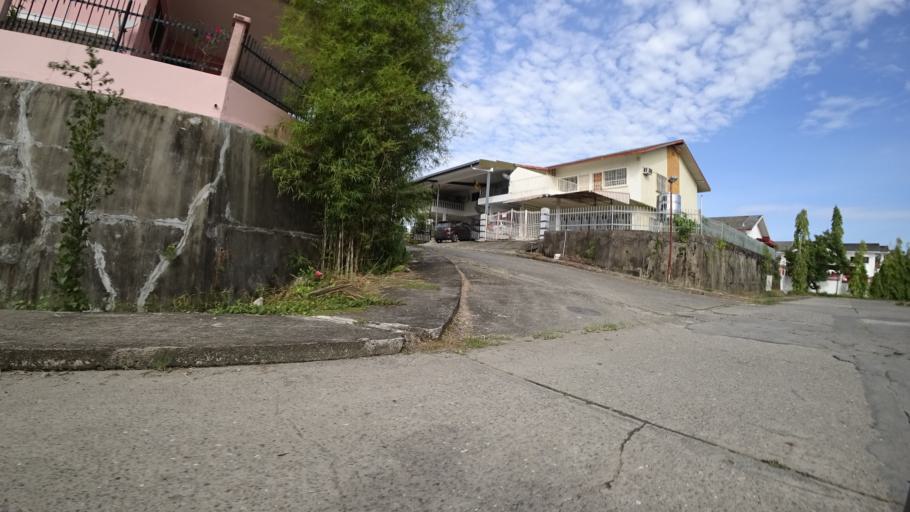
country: BN
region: Brunei and Muara
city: Bandar Seri Begawan
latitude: 4.8872
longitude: 114.9237
